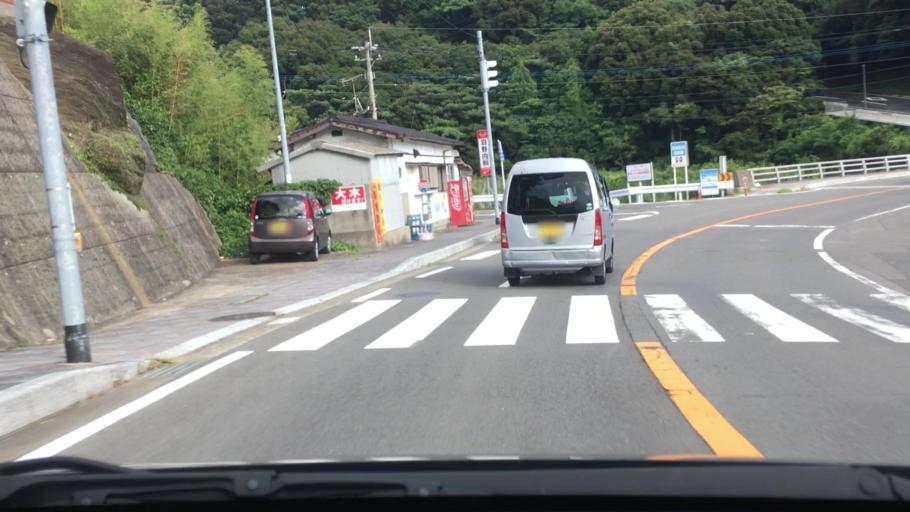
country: JP
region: Nagasaki
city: Togitsu
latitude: 32.8390
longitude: 129.7152
